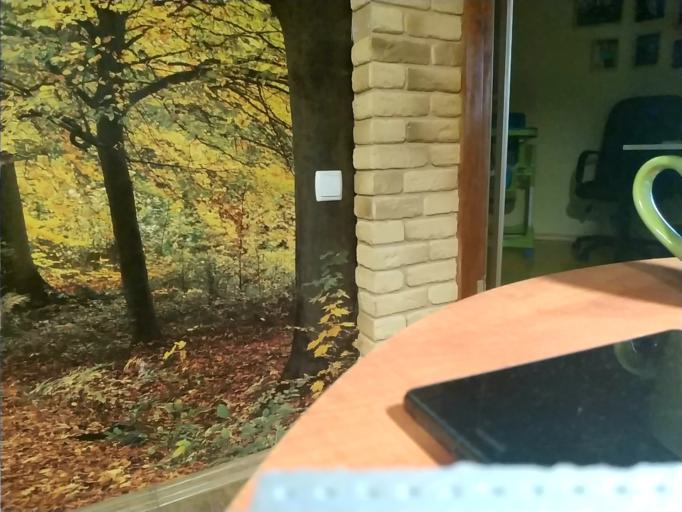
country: RU
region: Moskovskaya
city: Klin
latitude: 56.3580
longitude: 36.7532
